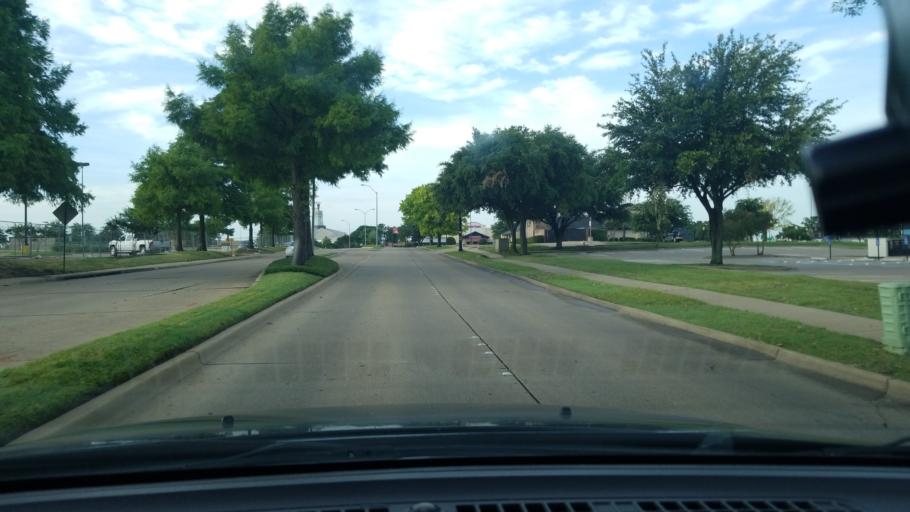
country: US
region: Texas
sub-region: Dallas County
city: Mesquite
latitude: 32.8138
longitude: -96.6260
